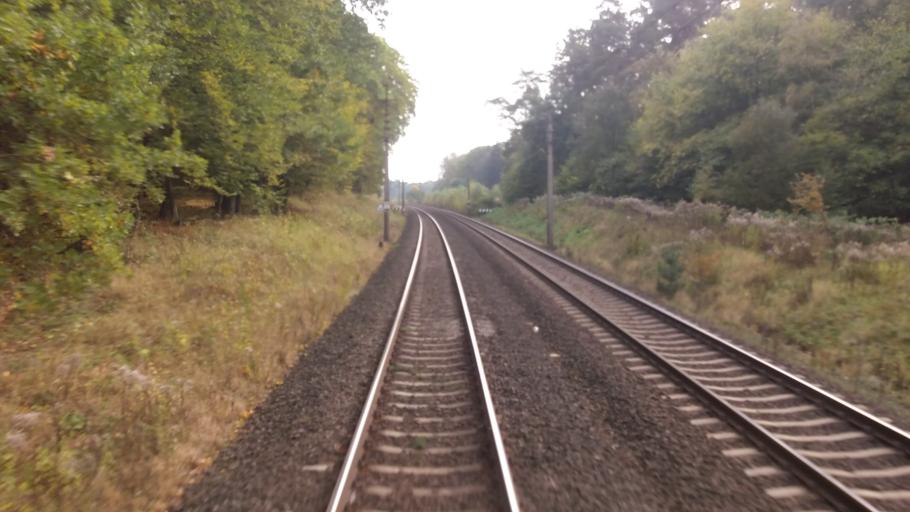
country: PL
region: West Pomeranian Voivodeship
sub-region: Powiat stargardzki
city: Dolice
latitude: 53.1710
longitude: 15.2902
